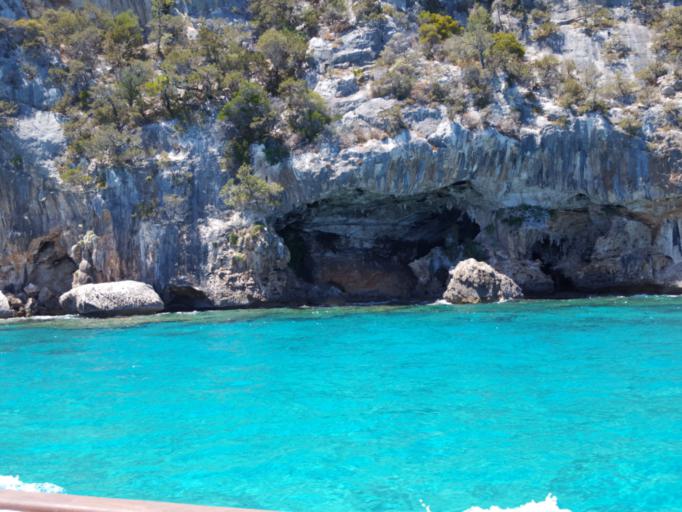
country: IT
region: Sardinia
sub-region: Provincia di Nuoro
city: Cala Gonone
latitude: 40.2478
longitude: 9.6238
